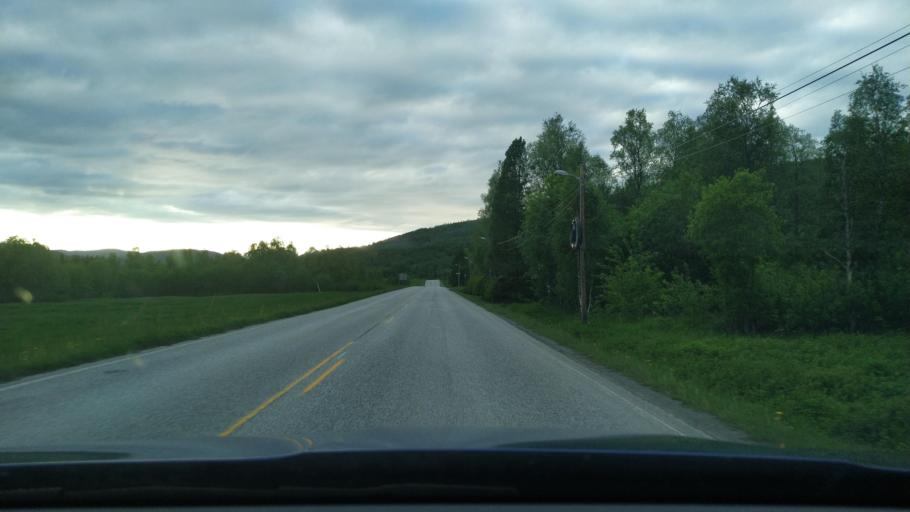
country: NO
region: Troms
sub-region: Sorreisa
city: Sorreisa
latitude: 69.1225
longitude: 18.2195
